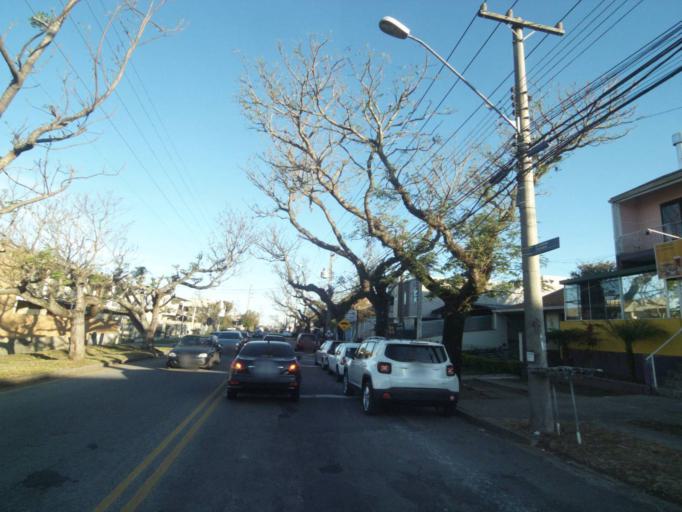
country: BR
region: Parana
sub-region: Curitiba
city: Curitiba
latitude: -25.3824
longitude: -49.2516
